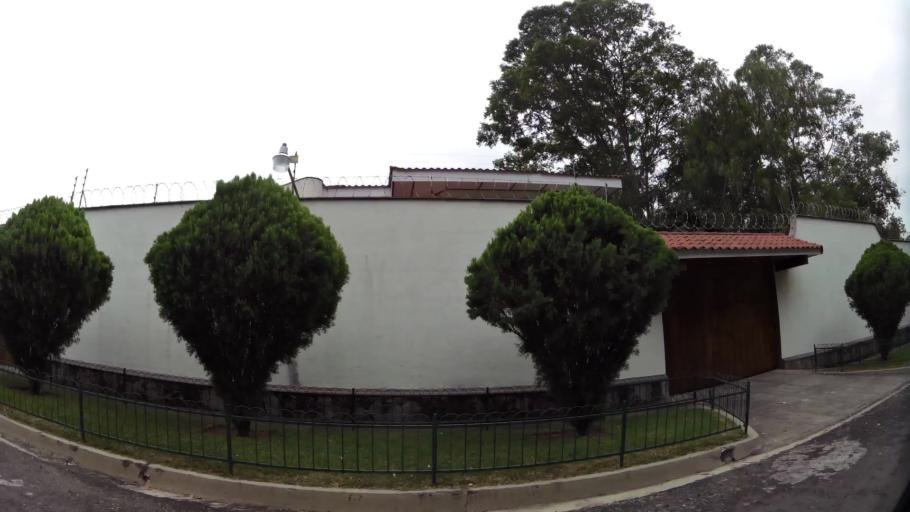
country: SV
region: San Salvador
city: Mejicanos
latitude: 13.7182
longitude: -89.2469
